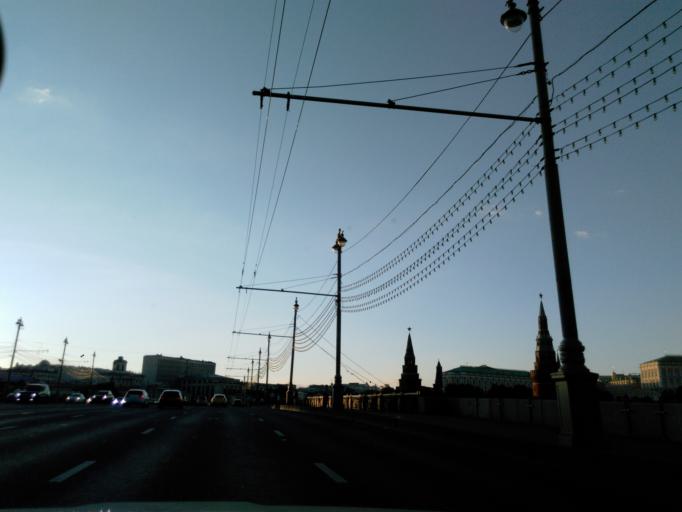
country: RU
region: Moscow
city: Moscow
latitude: 55.7458
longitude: 37.6133
